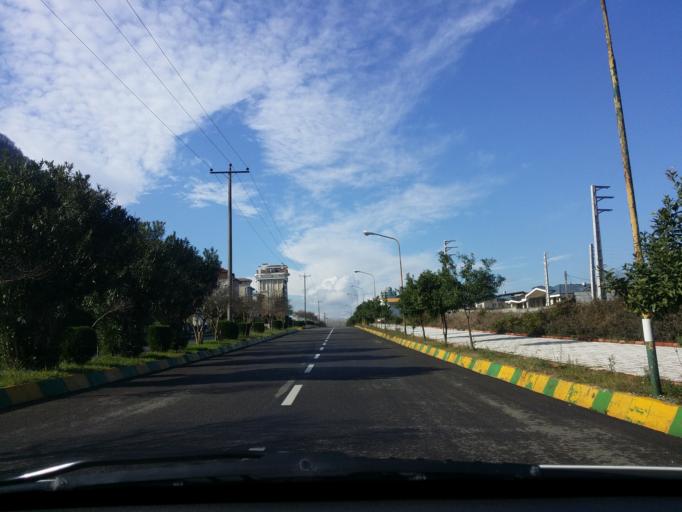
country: IR
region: Mazandaran
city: Chalus
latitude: 36.6667
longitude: 51.3149
